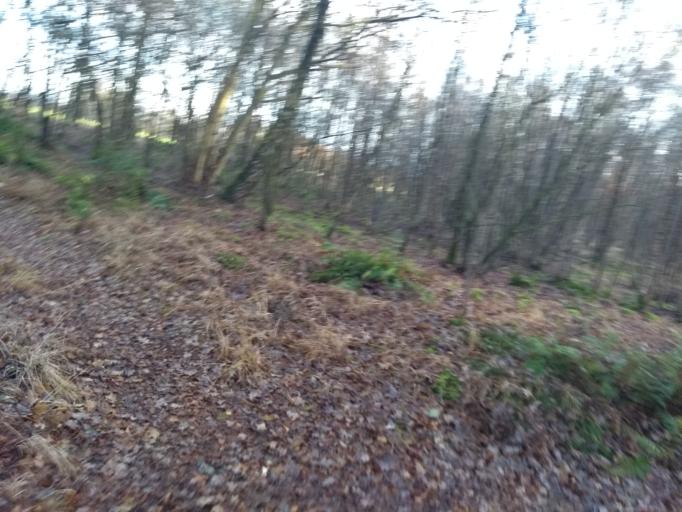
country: NL
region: Overijssel
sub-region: Gemeente Twenterand
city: Westerhaar-Vriezenveensewijk
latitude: 52.4509
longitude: 6.6763
